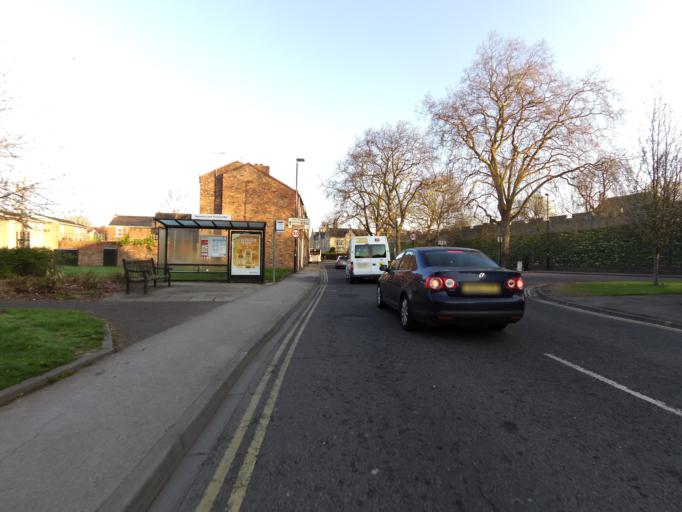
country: GB
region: England
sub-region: City of York
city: York
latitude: 53.9533
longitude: -1.0862
